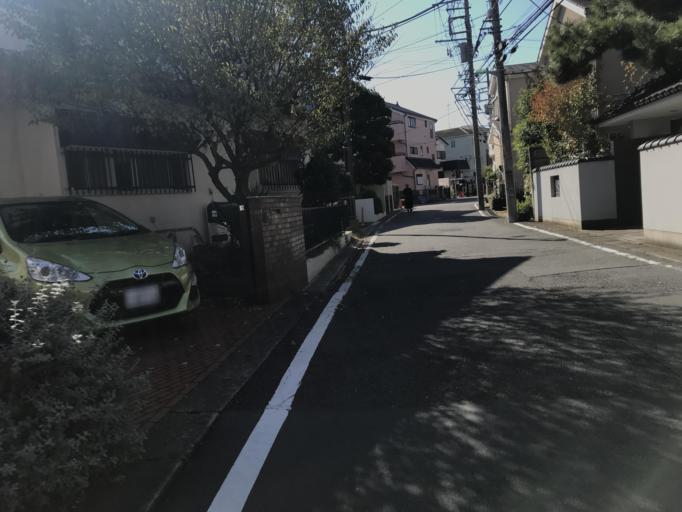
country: JP
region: Tokyo
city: Chofugaoka
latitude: 35.5803
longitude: 139.5784
